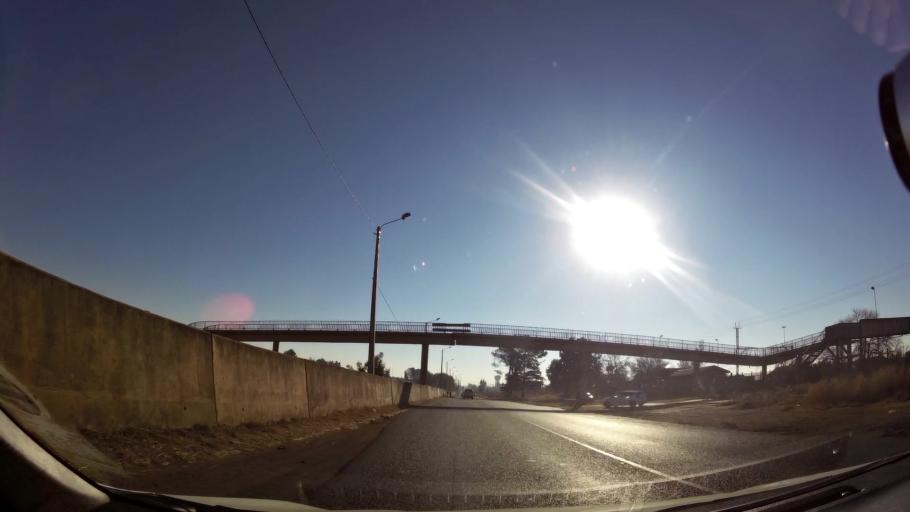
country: ZA
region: Gauteng
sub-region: Ekurhuleni Metropolitan Municipality
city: Germiston
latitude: -26.3509
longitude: 28.1254
